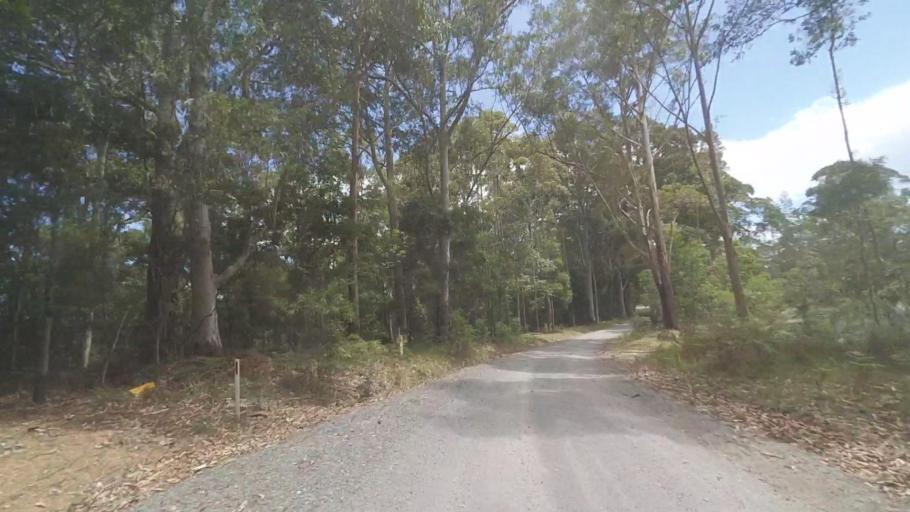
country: AU
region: New South Wales
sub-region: Shoalhaven Shire
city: Milton
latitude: -35.4427
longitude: 150.2956
